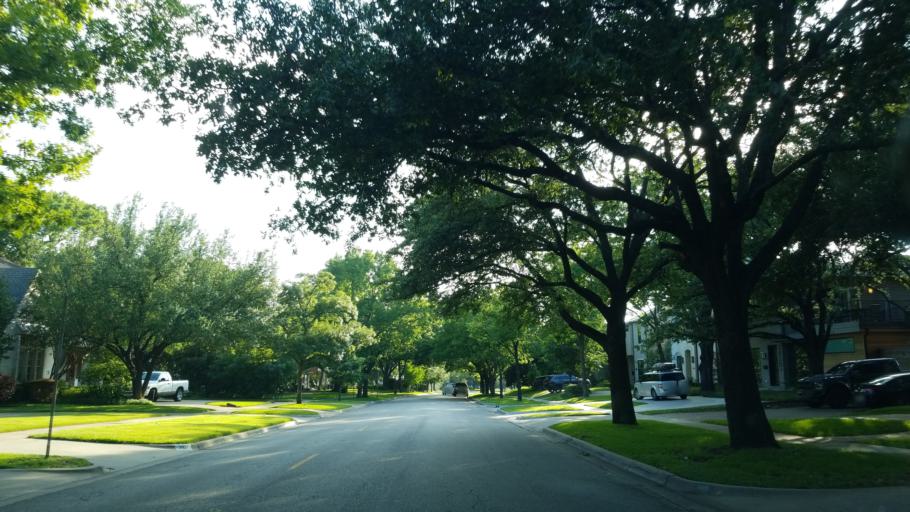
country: US
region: Texas
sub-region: Dallas County
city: Highland Park
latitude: 32.8452
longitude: -96.7882
